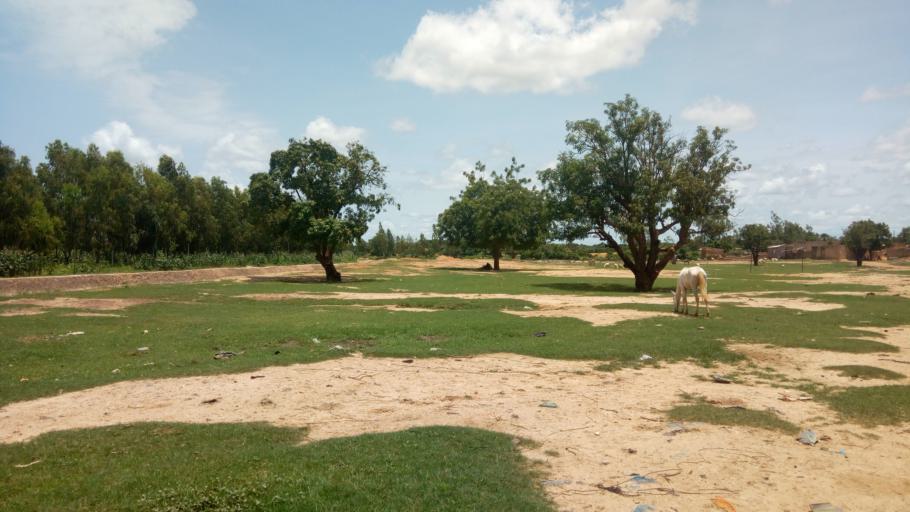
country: ML
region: Sikasso
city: Koutiala
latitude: 12.3897
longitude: -5.4598
